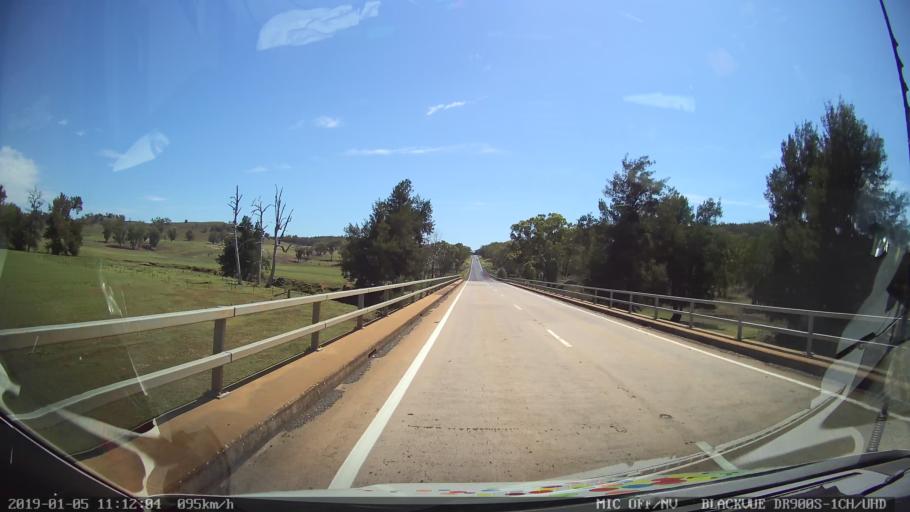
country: AU
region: New South Wales
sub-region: Warrumbungle Shire
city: Coonabarabran
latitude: -31.3859
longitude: 149.2565
